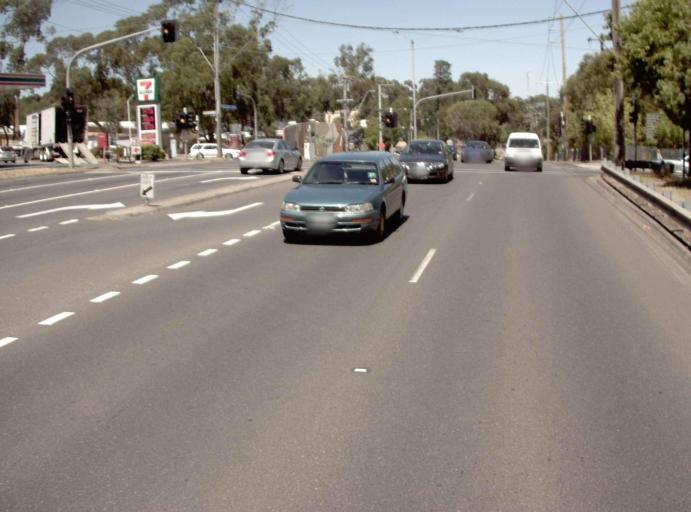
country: AU
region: Victoria
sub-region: Yarra Ranges
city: Tremont
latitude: -37.9019
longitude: 145.3295
